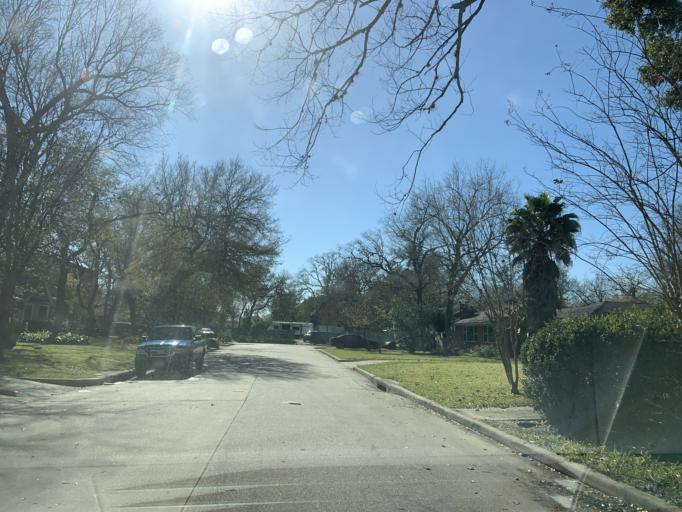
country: US
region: Texas
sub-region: Harris County
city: Bellaire
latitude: 29.6779
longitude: -95.5108
